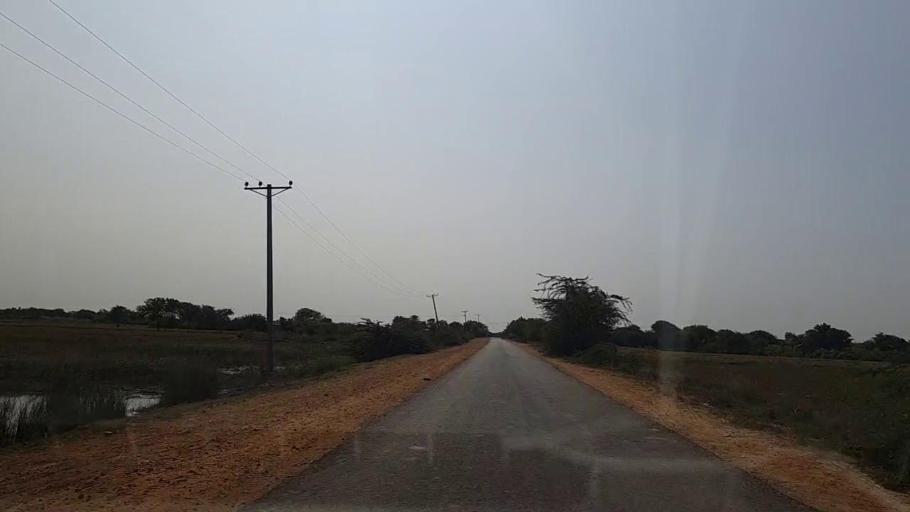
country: PK
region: Sindh
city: Chuhar Jamali
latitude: 24.3259
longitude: 67.9428
